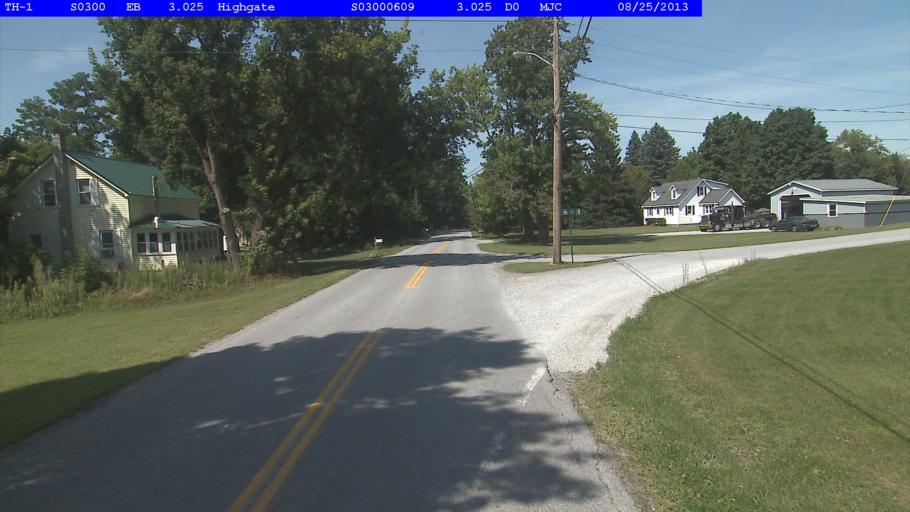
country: US
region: Vermont
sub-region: Franklin County
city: Swanton
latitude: 44.9649
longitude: -73.1002
